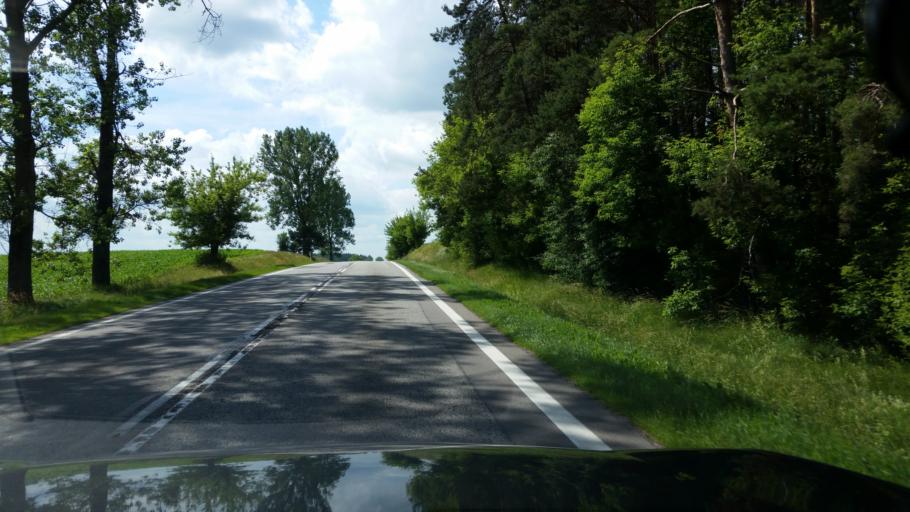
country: PL
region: Podlasie
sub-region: Powiat lomzynski
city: Piatnica
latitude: 53.2823
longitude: 22.1387
